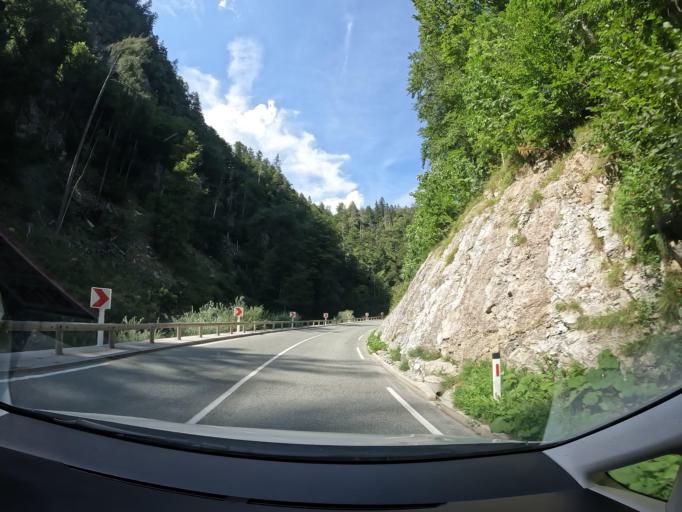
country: SI
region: Trzic
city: Trzic
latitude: 46.4023
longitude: 14.3290
